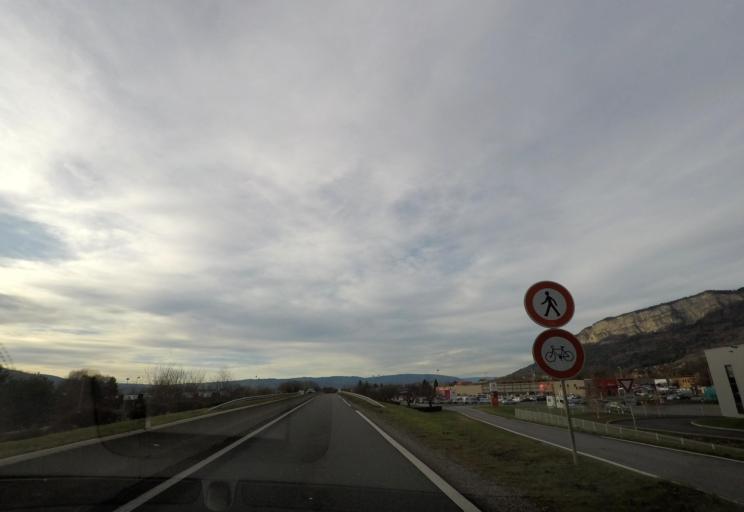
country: FR
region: Rhone-Alpes
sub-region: Departement de la Haute-Savoie
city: Ayse
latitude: 46.0719
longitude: 6.4219
